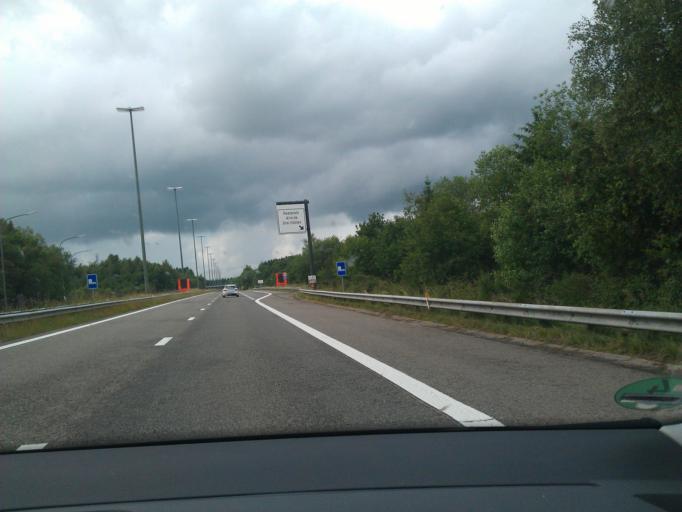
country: DE
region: Rheinland-Pfalz
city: Winterspelt
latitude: 50.2474
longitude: 6.1740
